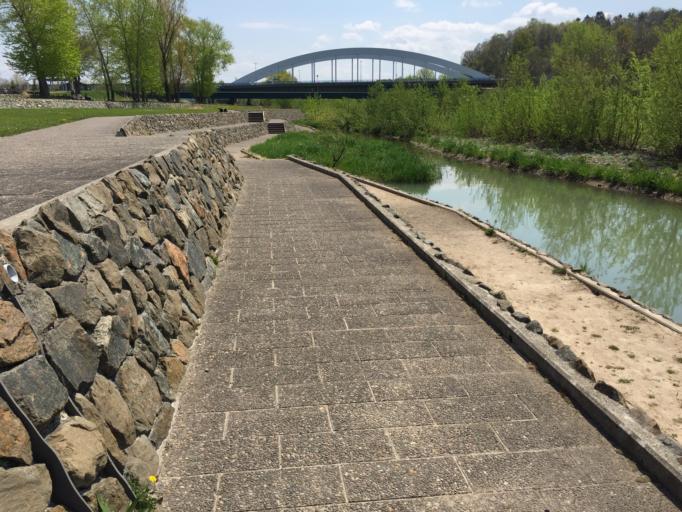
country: JP
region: Hokkaido
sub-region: Asahikawa-shi
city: Asahikawa
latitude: 43.7571
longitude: 142.3650
